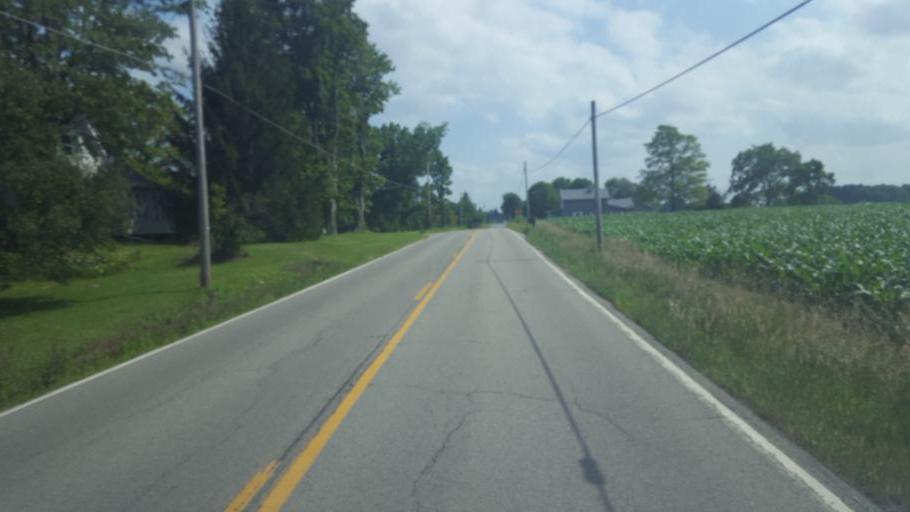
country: US
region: Ohio
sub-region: Richland County
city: Shelby
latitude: 40.9177
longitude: -82.7722
